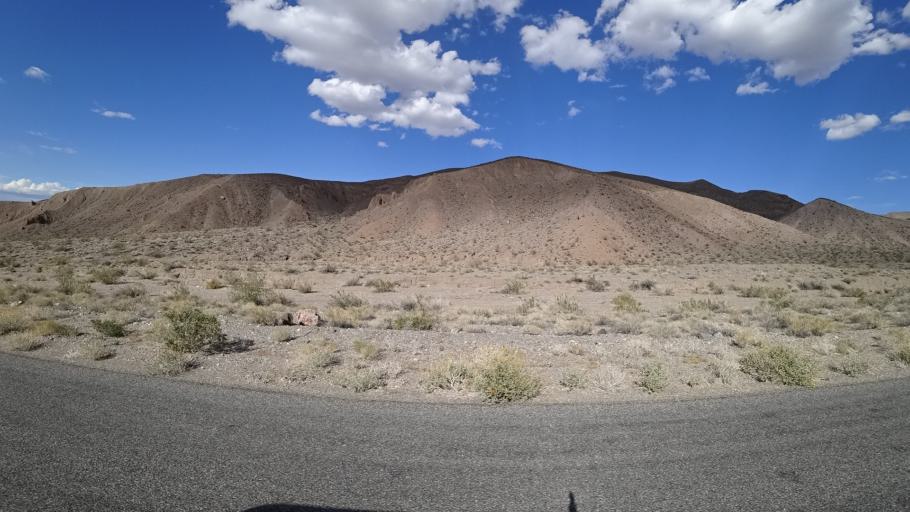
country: US
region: Nevada
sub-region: Nye County
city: Beatty
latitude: 36.4544
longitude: -117.2061
